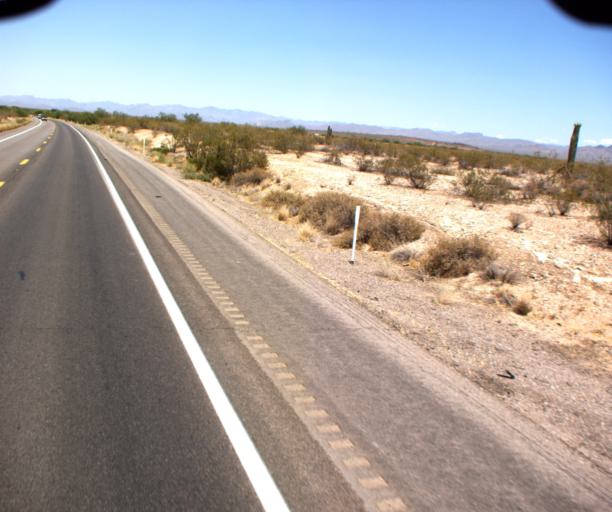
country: US
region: Arizona
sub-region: Pinal County
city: Florence
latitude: 33.1212
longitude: -111.3614
